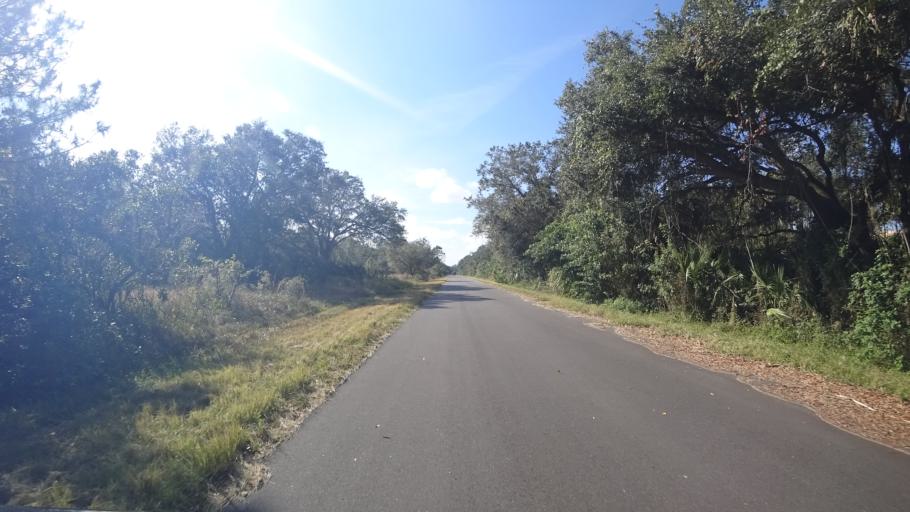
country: US
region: Florida
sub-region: Charlotte County
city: Port Charlotte
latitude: 27.0674
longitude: -82.1159
